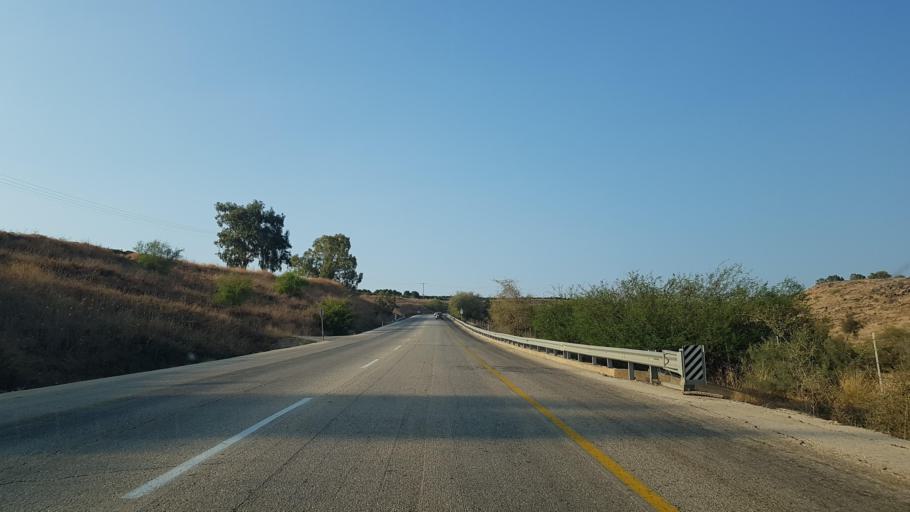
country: SY
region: Quneitra
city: Al Butayhah
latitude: 32.8957
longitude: 35.5975
